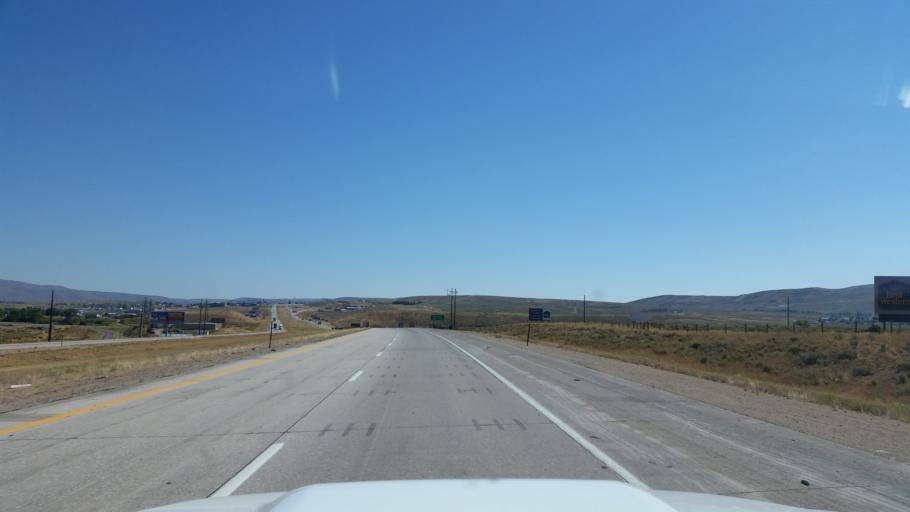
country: US
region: Wyoming
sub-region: Uinta County
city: Evanston
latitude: 41.2479
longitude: -111.0141
